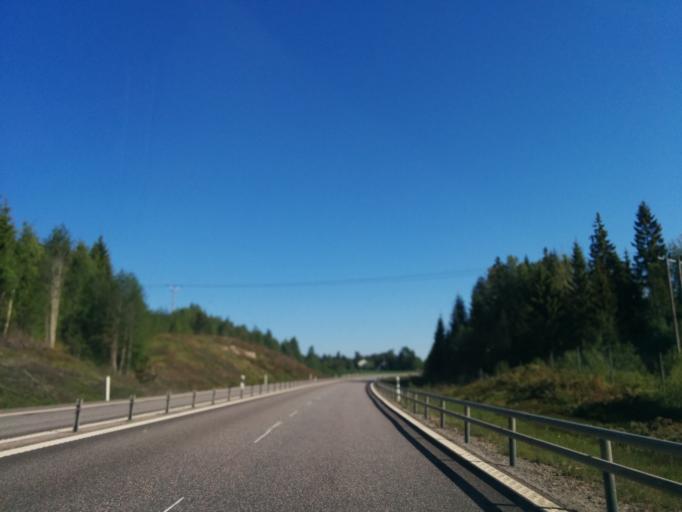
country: SE
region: Vaesternorrland
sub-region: Haernoesands Kommun
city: Haernoesand
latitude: 62.7528
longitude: 17.9022
